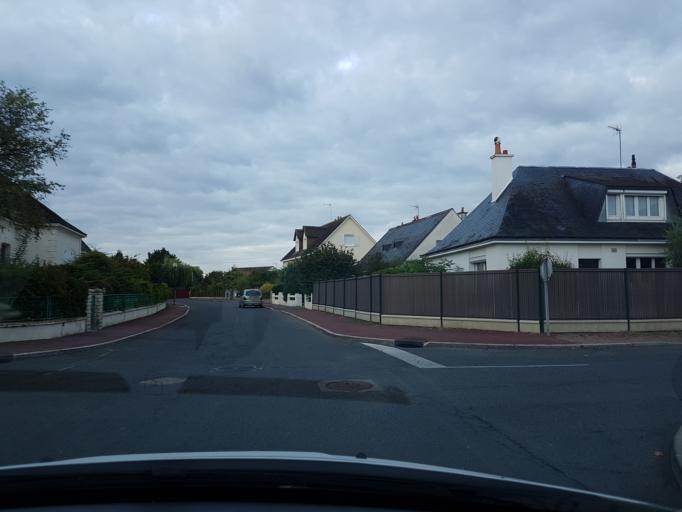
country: FR
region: Centre
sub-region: Departement d'Indre-et-Loire
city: Chambray-les-Tours
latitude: 47.3355
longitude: 0.7087
